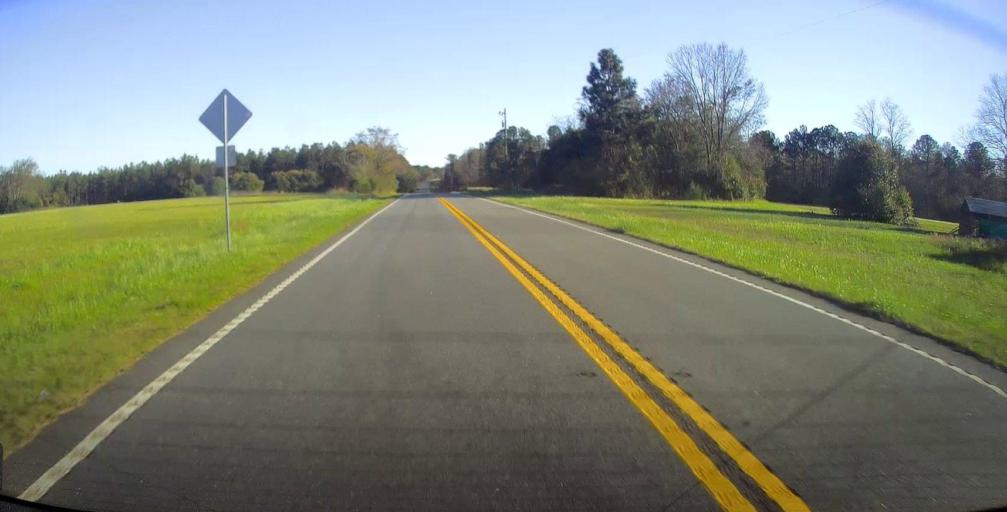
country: US
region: Georgia
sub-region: Taylor County
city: Butler
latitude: 32.4953
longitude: -84.4000
